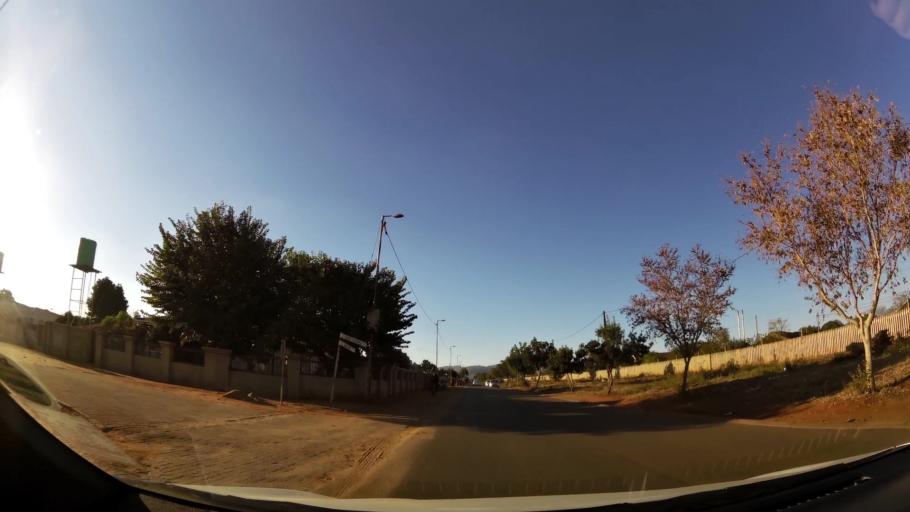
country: ZA
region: Limpopo
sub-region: Waterberg District Municipality
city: Mokopane
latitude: -24.1538
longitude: 28.9857
